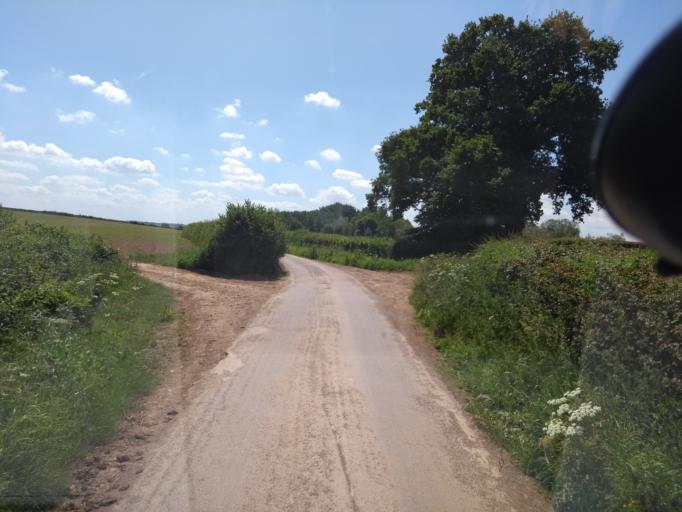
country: GB
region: England
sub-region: Somerset
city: North Petherton
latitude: 51.0541
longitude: -2.9994
